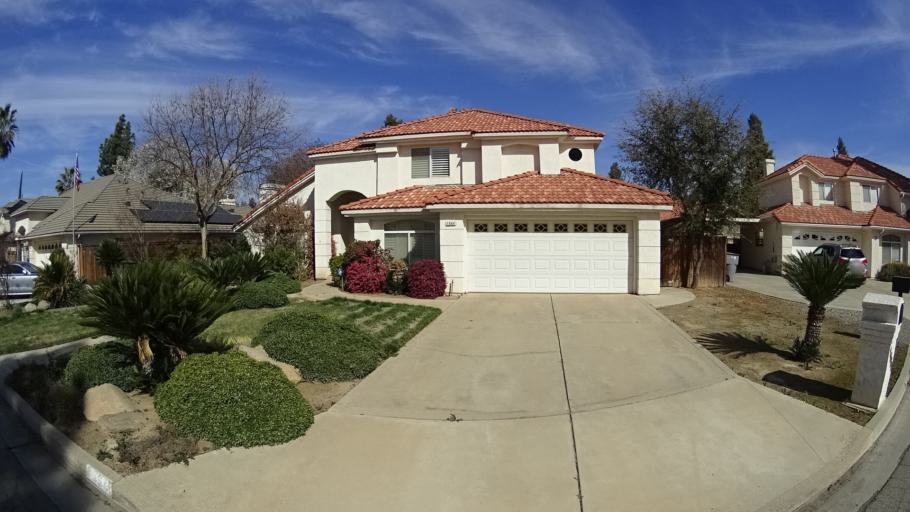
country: US
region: California
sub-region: Fresno County
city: Clovis
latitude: 36.8538
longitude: -119.7530
